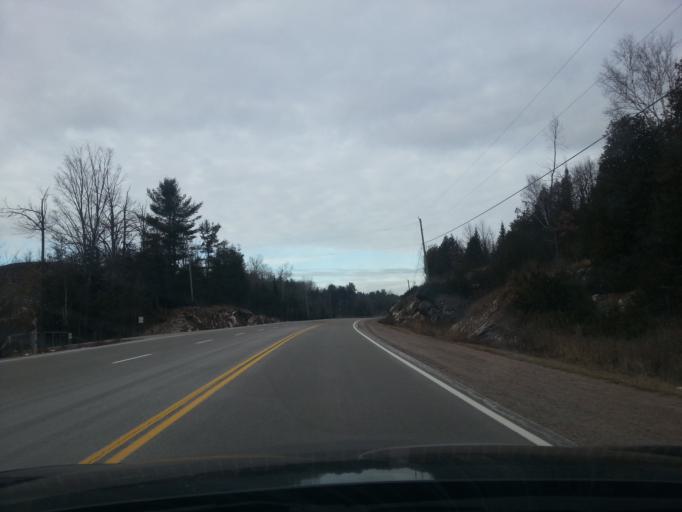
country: CA
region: Ontario
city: Belleville
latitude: 44.5574
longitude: -77.2915
